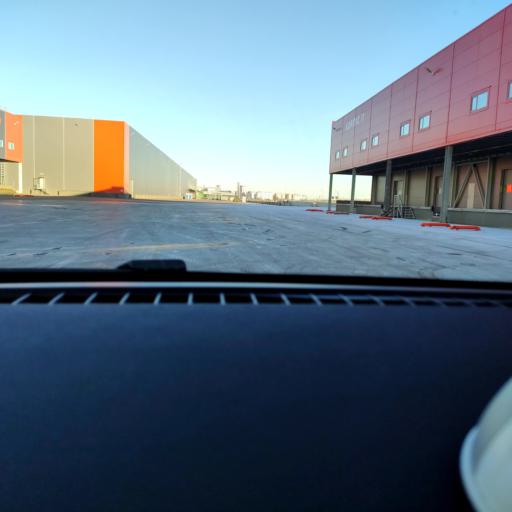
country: RU
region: Samara
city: Samara
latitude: 53.0910
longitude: 50.1276
